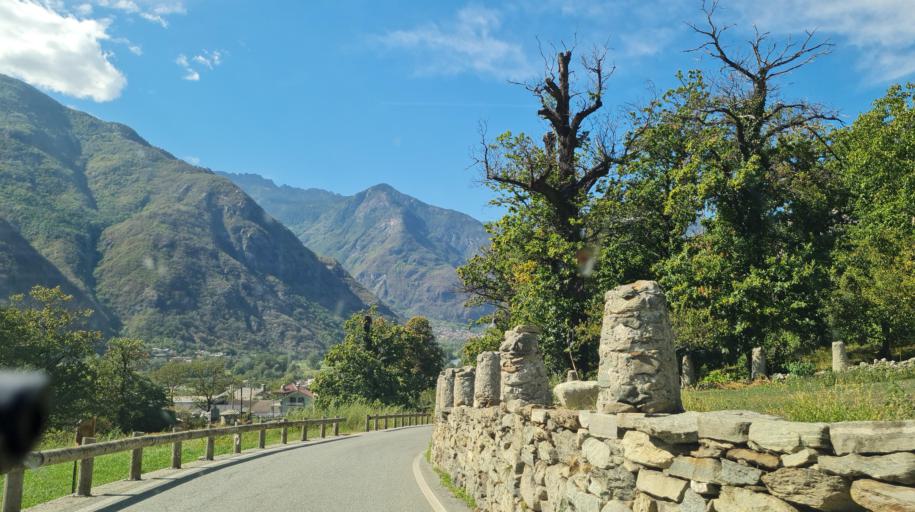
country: IT
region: Aosta Valley
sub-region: Valle d'Aosta
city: Arnad
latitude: 45.6393
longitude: 7.7296
